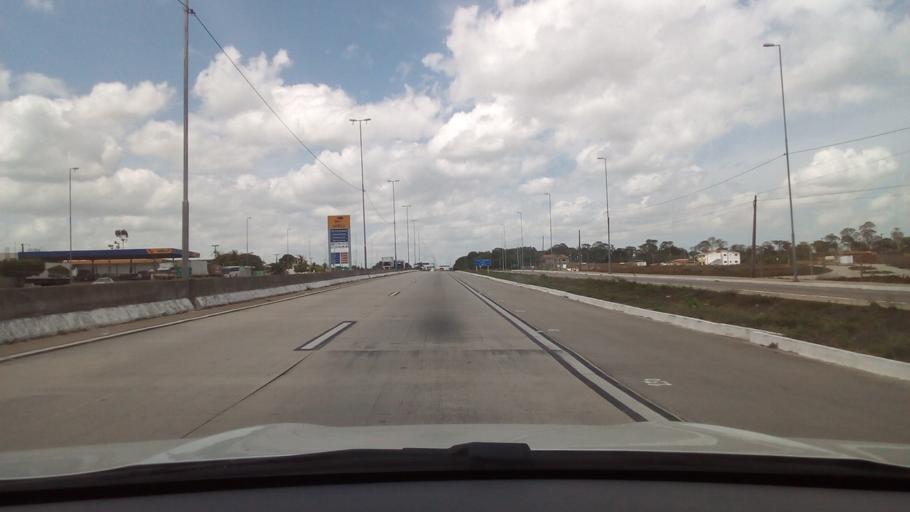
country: BR
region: Paraiba
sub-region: Mamanguape
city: Mamanguape
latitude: -6.8288
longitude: -35.1376
